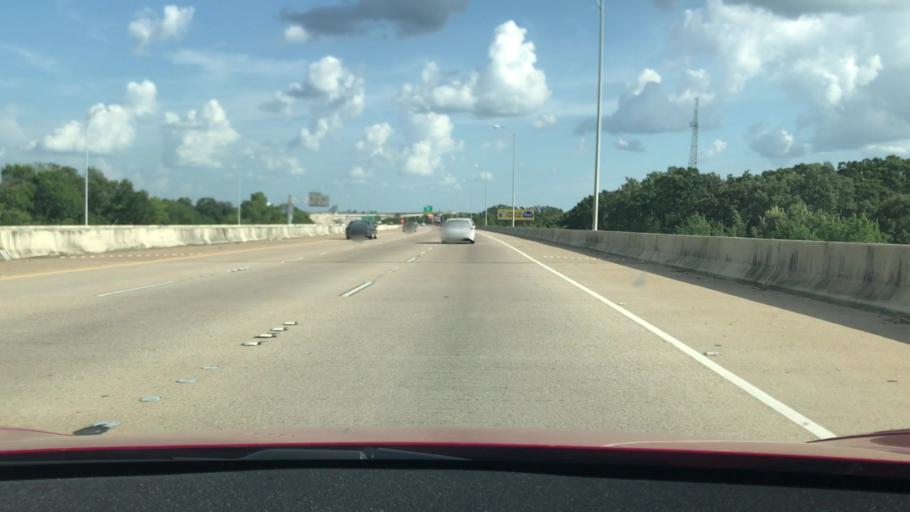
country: US
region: Louisiana
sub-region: Bossier Parish
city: Bossier City
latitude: 32.4336
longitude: -93.7552
